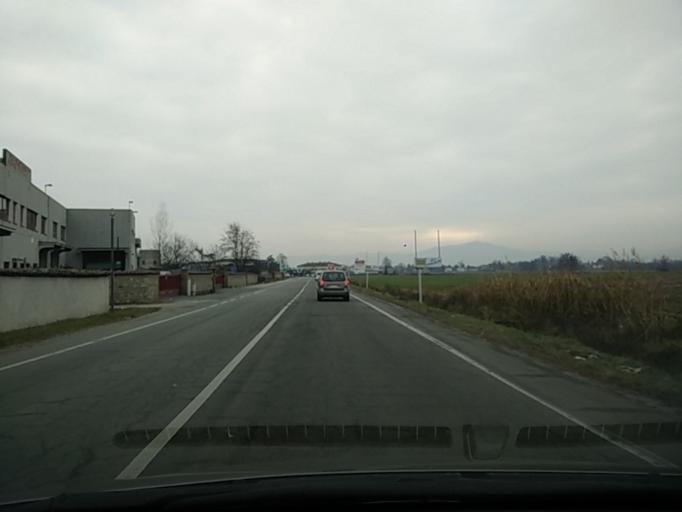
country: IT
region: Piedmont
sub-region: Provincia di Torino
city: Leini
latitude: 45.1602
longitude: 7.7126
